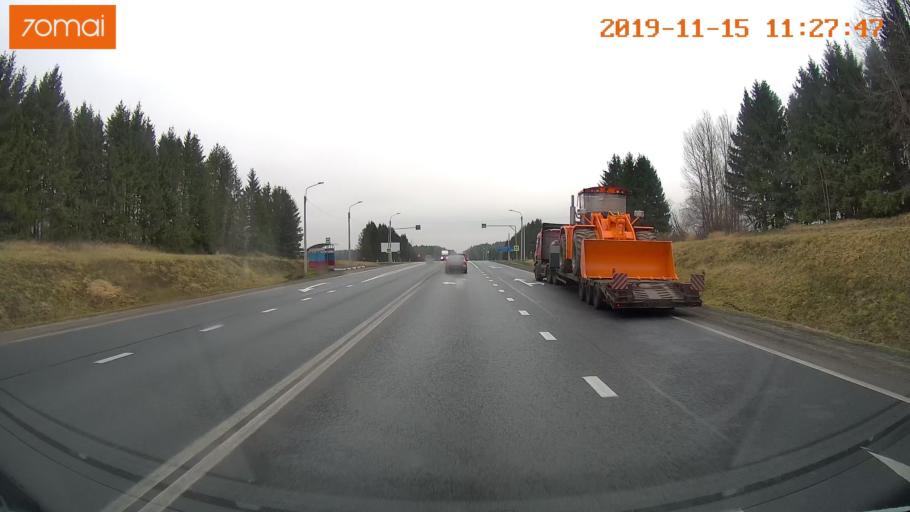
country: RU
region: Vologda
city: Molochnoye
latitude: 59.1705
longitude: 39.4732
